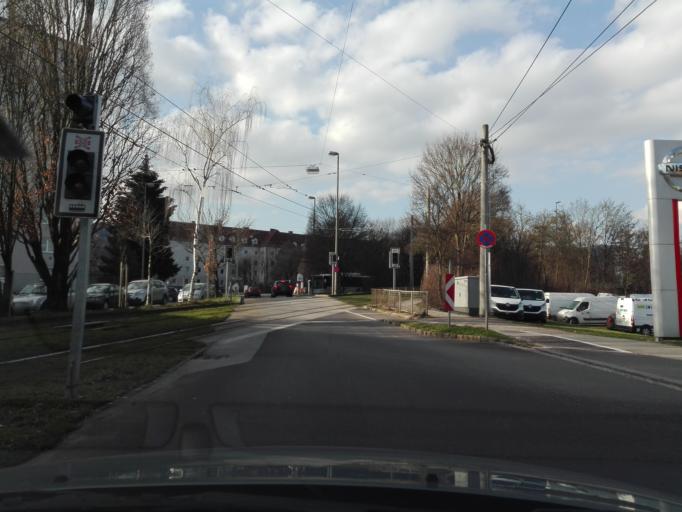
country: AT
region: Upper Austria
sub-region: Linz Stadt
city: Linz
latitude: 48.3229
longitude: 14.2848
